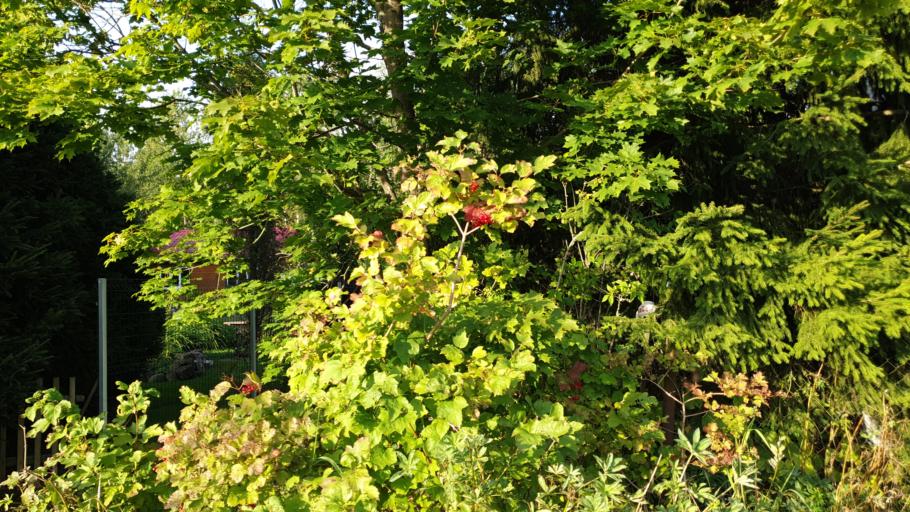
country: RU
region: Leningrad
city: Ivangorod
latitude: 59.4262
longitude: 28.3293
